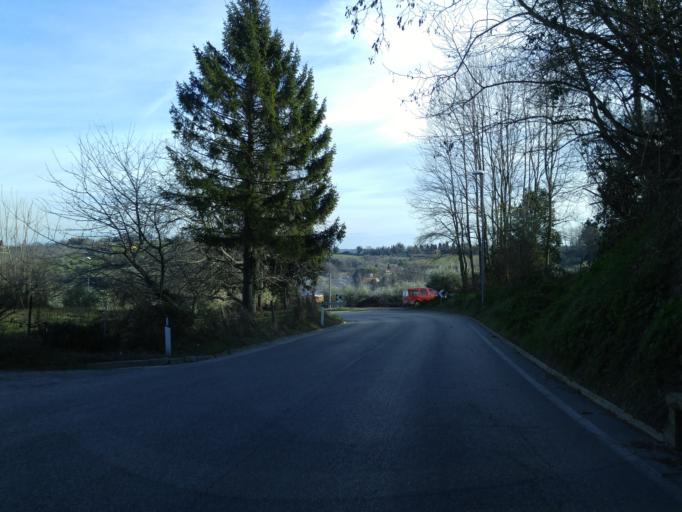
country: IT
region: The Marches
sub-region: Provincia di Pesaro e Urbino
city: Cartoceto
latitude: 43.7669
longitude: 12.8792
